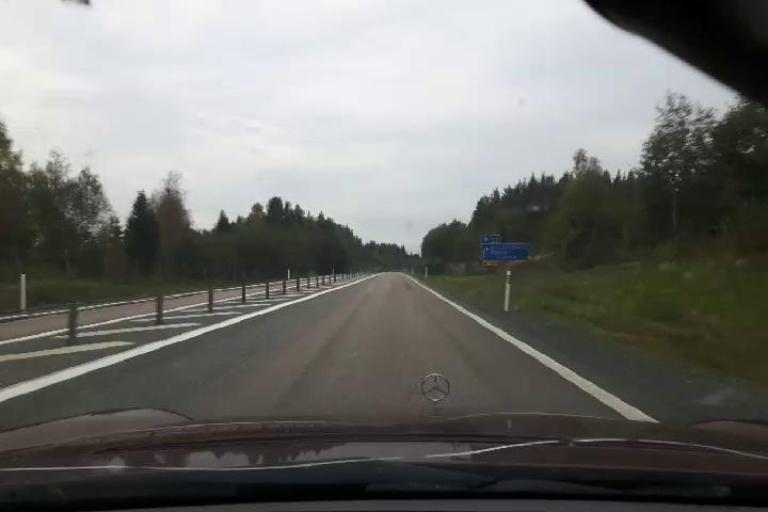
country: SE
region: Vaesternorrland
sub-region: Haernoesands Kommun
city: Haernoesand
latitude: 62.8630
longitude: 18.0328
